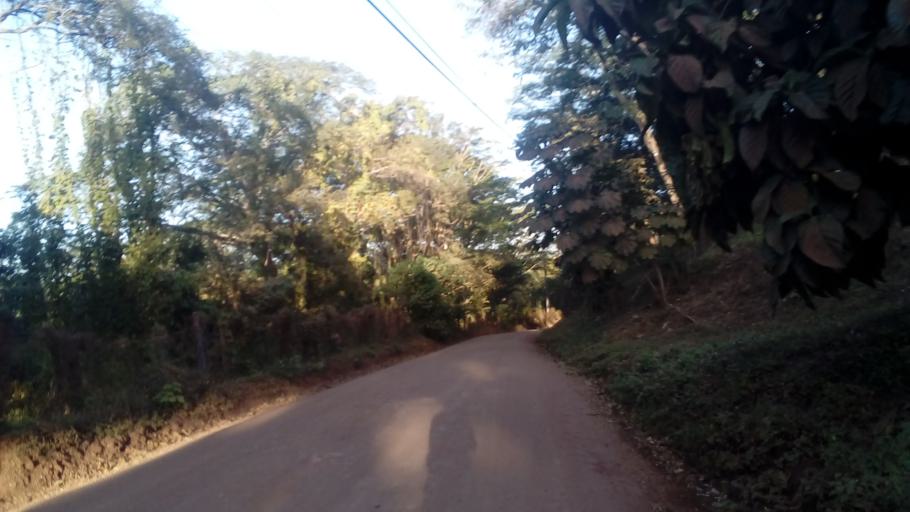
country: CR
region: Guanacaste
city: Sardinal
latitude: 10.3943
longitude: -85.8206
